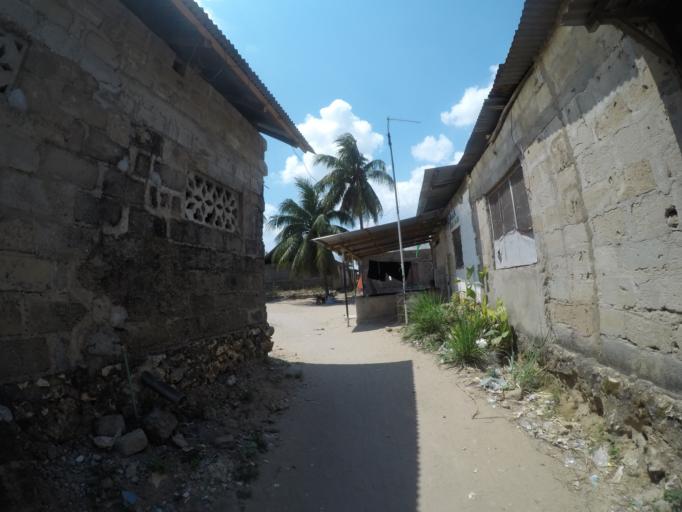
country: TZ
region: Zanzibar Urban/West
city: Zanzibar
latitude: -6.1772
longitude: 39.2078
